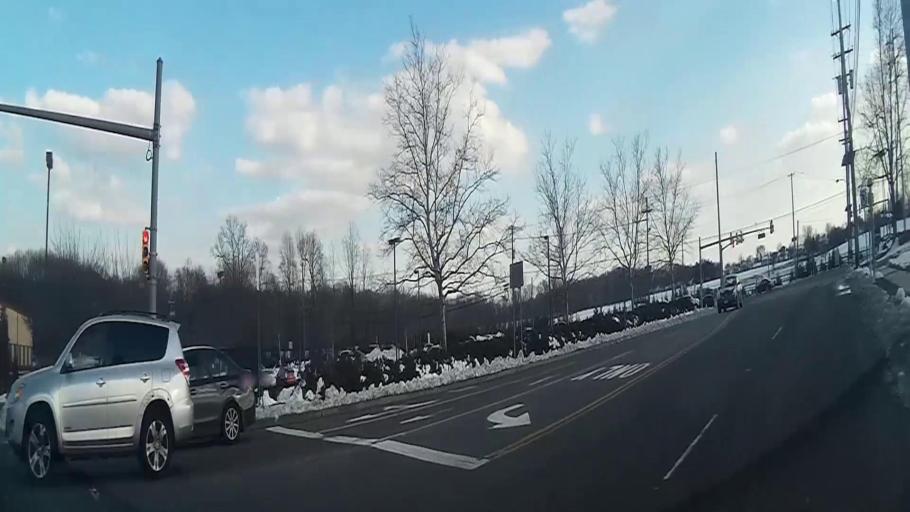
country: US
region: New Jersey
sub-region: Camden County
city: Echelon
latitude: 39.8620
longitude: -74.9756
